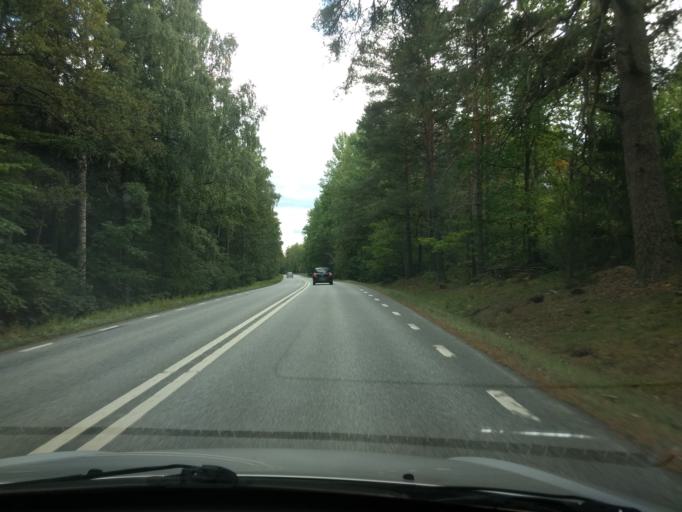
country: SE
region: Uppsala
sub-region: Uppsala Kommun
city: Saevja
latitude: 59.7490
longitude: 17.6531
